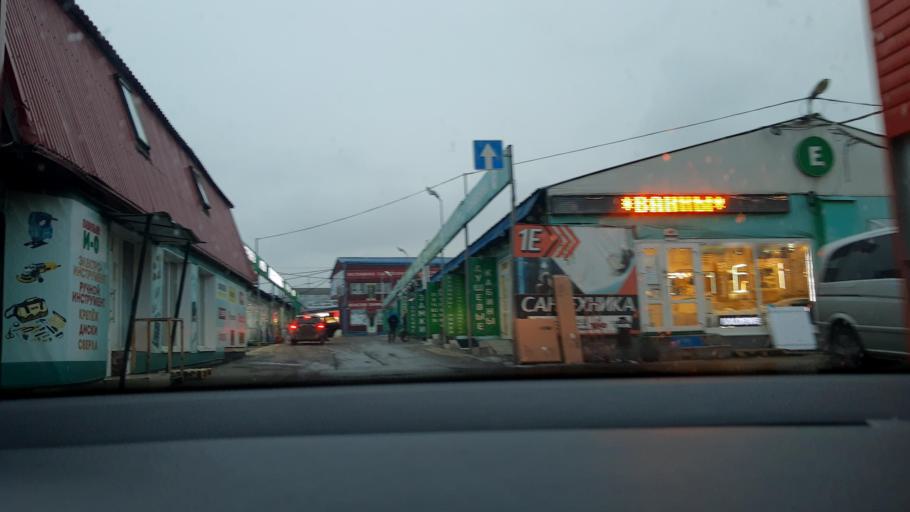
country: RU
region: Moskovskaya
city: Reutov
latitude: 55.7785
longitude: 37.8550
